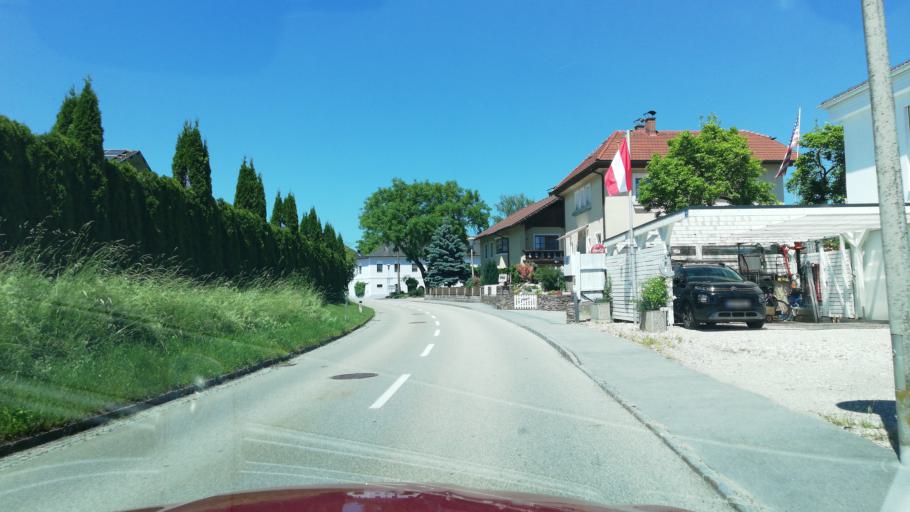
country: AT
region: Upper Austria
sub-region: Wels-Land
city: Bachmanning
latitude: 48.1294
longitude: 13.7967
